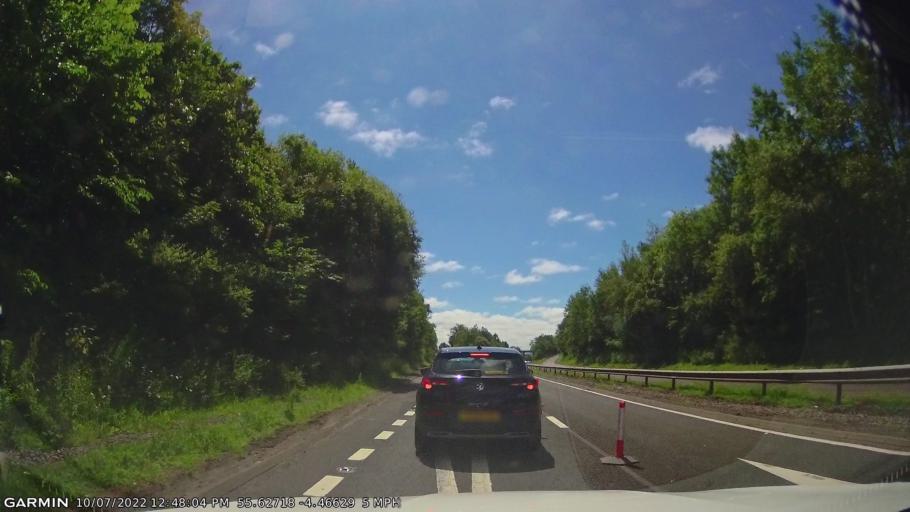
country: GB
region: Scotland
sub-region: East Ayrshire
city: Kilmarnock
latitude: 55.6272
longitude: -4.4663
